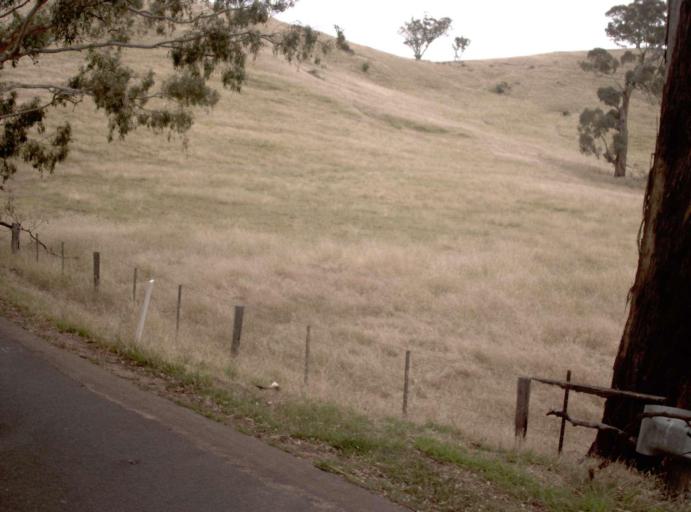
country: AU
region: Victoria
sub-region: Wellington
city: Heyfield
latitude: -37.6586
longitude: 146.6457
